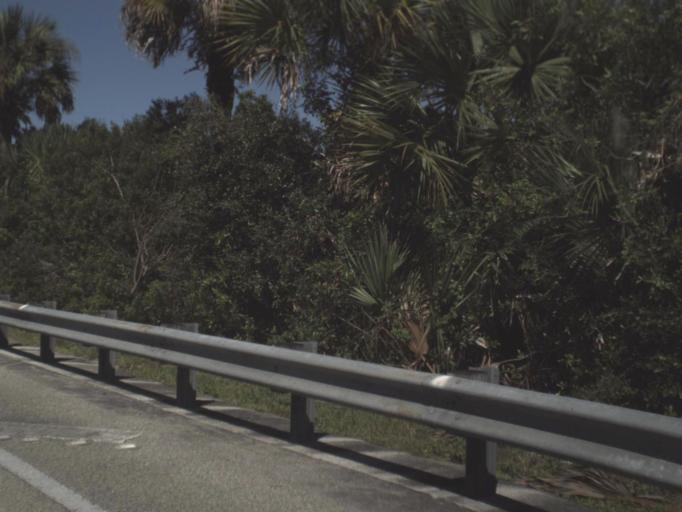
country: US
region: Florida
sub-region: Collier County
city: Marco
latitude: 25.9604
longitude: -81.5152
